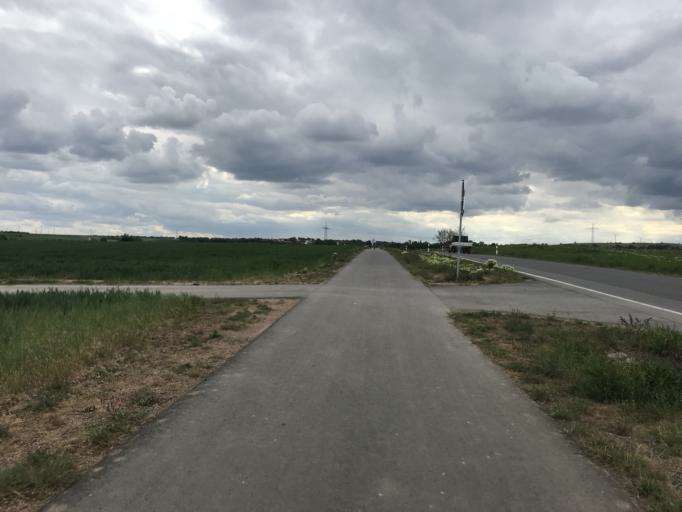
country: DE
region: Rheinland-Pfalz
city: Lorzweiler
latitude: 49.8936
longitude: 8.2881
